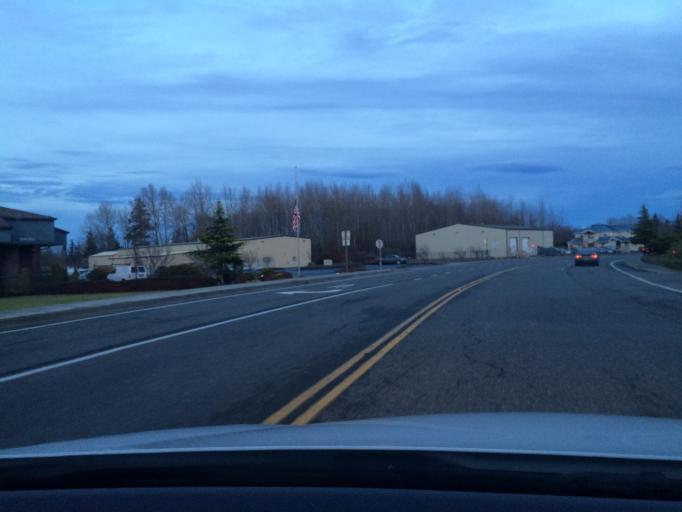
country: US
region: Washington
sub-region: Whatcom County
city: Marietta-Alderwood
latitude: 48.7857
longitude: -122.5256
